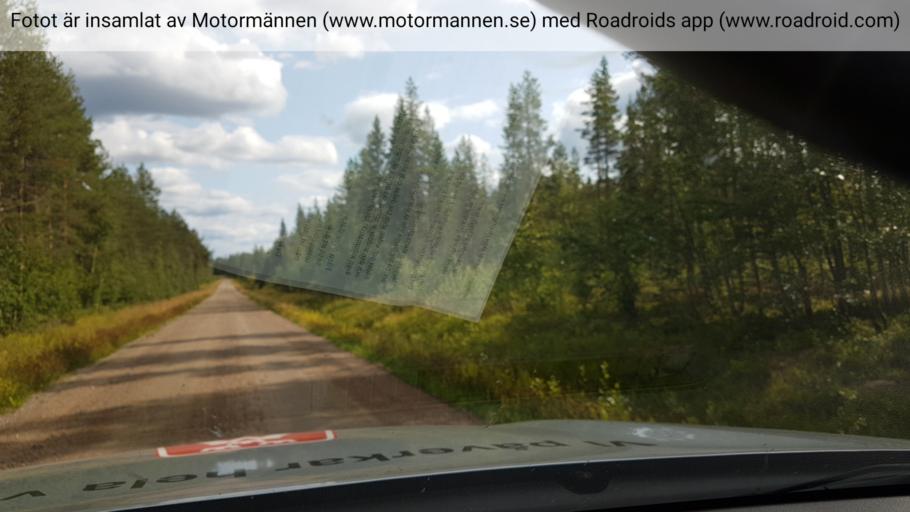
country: SE
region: Vaesterbotten
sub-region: Skelleftea Kommun
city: Langsele
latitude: 65.2166
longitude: 20.1290
